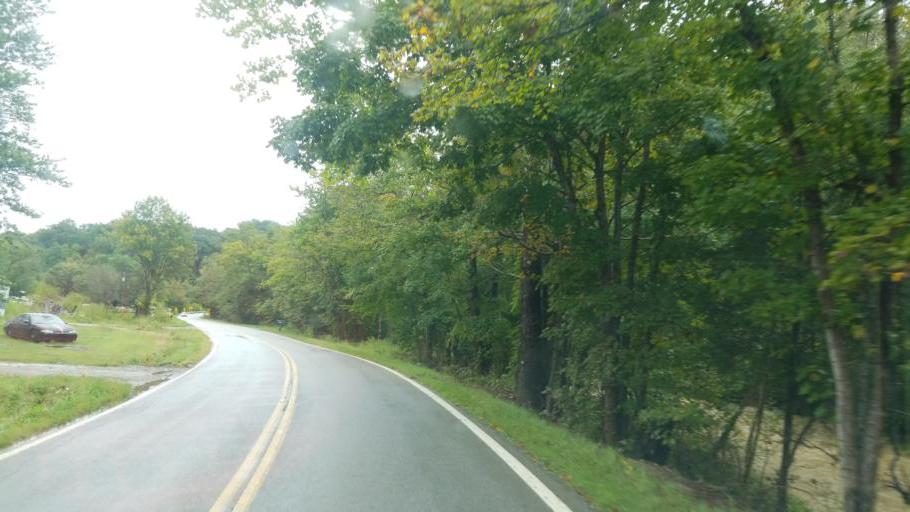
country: US
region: Ohio
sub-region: Adams County
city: West Union
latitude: 38.7668
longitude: -83.5270
